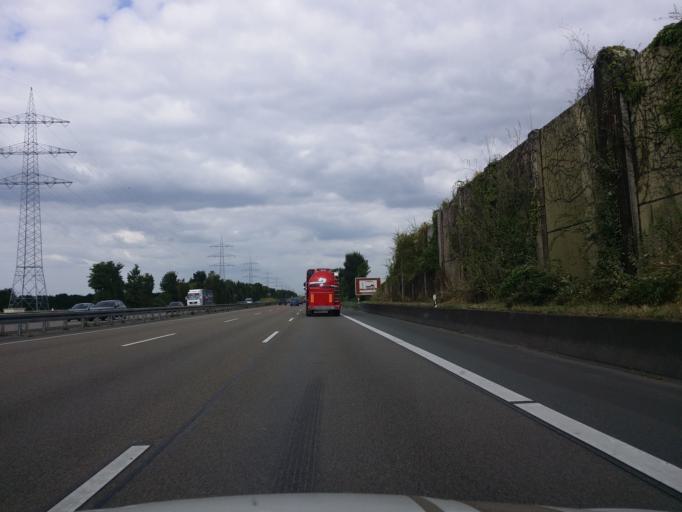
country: DE
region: Hesse
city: Liederbach
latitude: 50.1050
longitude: 8.5050
